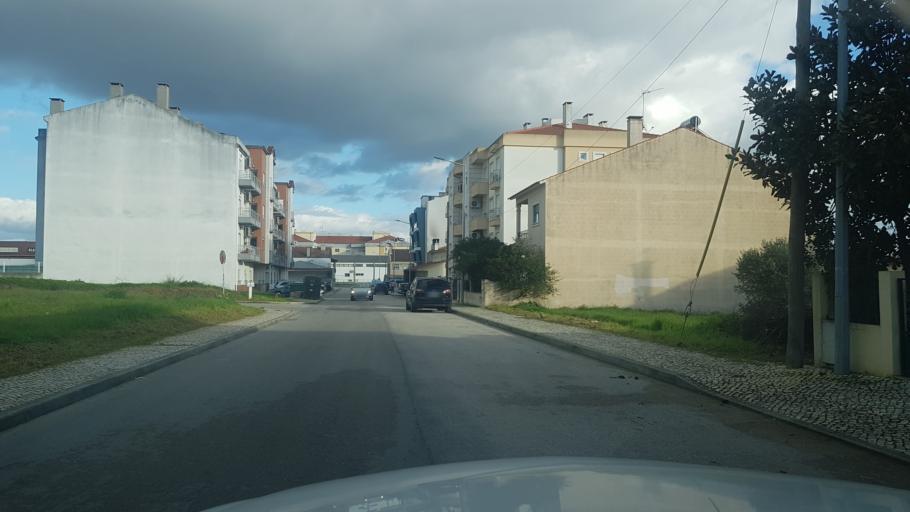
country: PT
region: Santarem
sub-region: Entroncamento
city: Entroncamento
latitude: 39.4745
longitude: -8.4754
